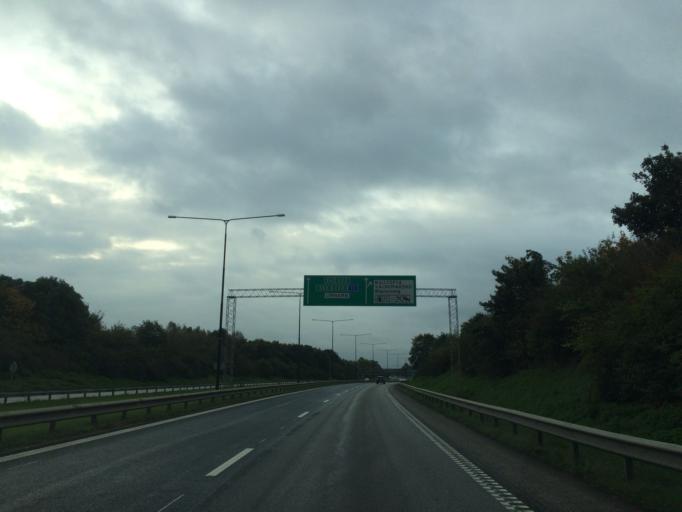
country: SE
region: Skane
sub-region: Burlovs Kommun
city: Arloev
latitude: 55.6162
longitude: 13.0626
